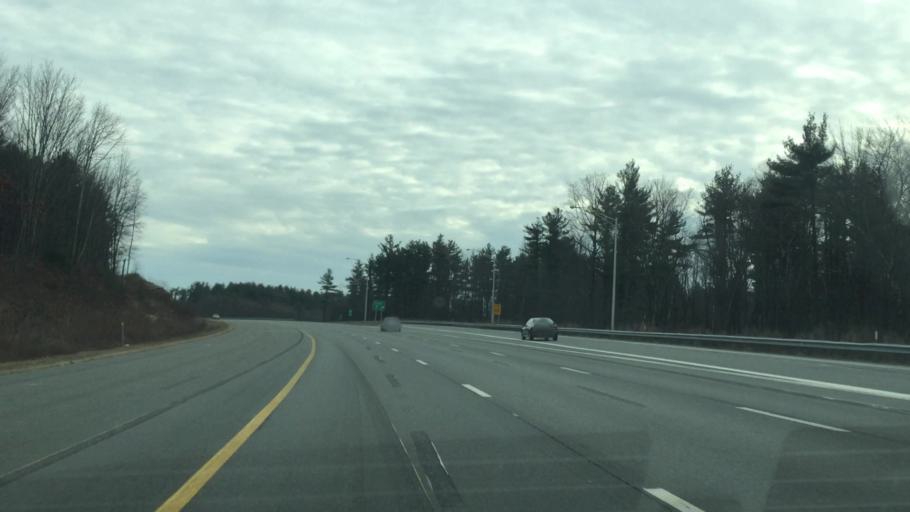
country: US
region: New Hampshire
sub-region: Rockingham County
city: Windham
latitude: 42.8166
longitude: -71.2860
